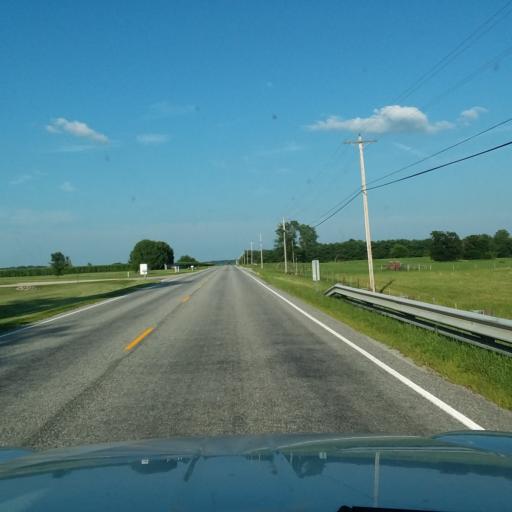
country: US
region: Indiana
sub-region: Johnson County
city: Princes Lakes
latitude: 39.4107
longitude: -86.0602
